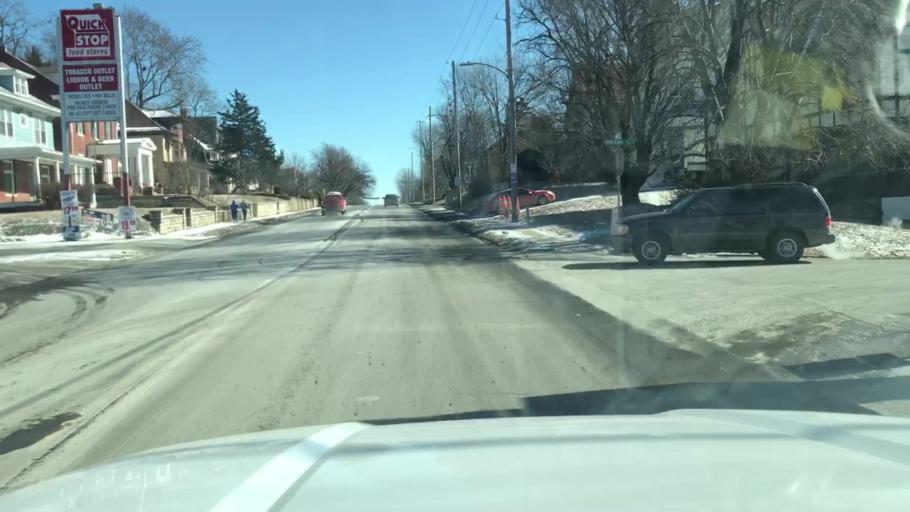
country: US
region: Missouri
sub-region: Buchanan County
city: Saint Joseph
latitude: 39.7768
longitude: -94.8293
